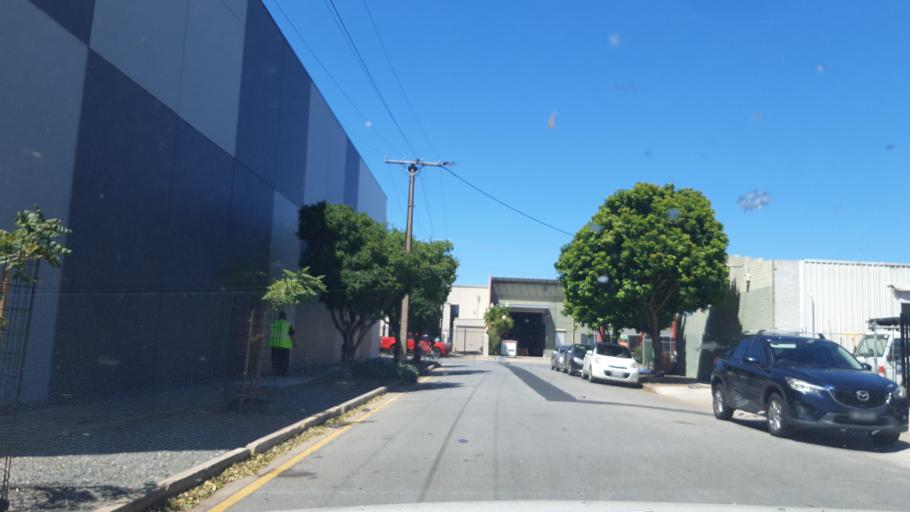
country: AU
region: South Australia
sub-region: Mitcham
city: Clarence Gardens
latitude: -34.9852
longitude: 138.5717
